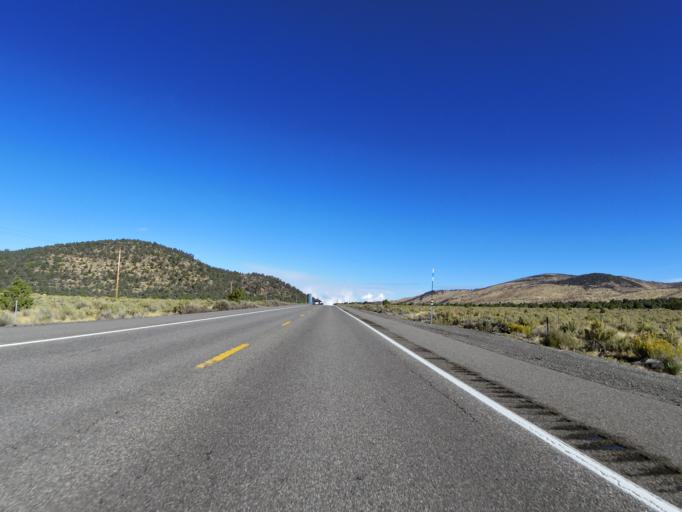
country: US
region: Nevada
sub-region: Douglas County
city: Gardnerville Ranchos
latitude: 38.7990
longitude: -119.6038
